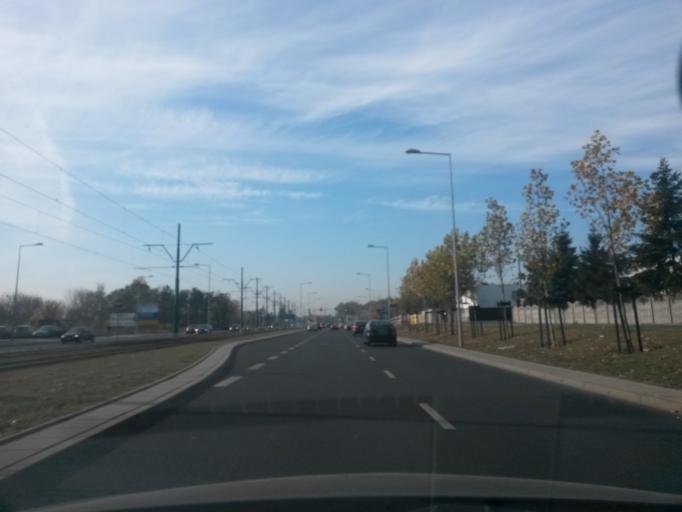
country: PL
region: Greater Poland Voivodeship
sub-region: Powiat poznanski
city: Plewiska
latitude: 52.3863
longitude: 16.8429
